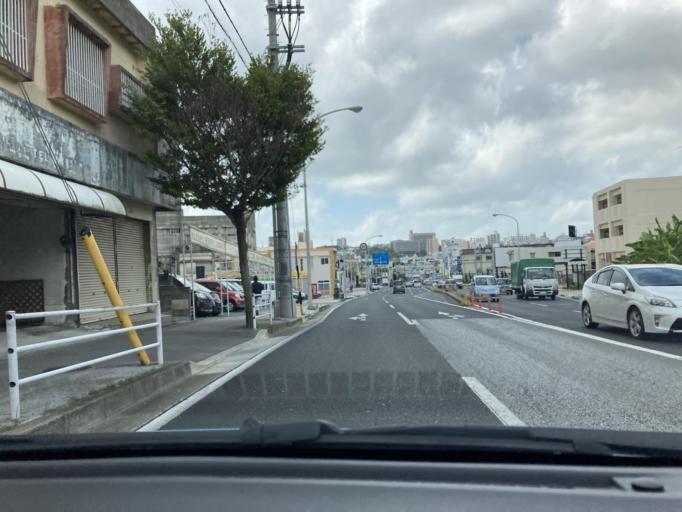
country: JP
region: Okinawa
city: Okinawa
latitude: 26.3398
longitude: 127.8167
